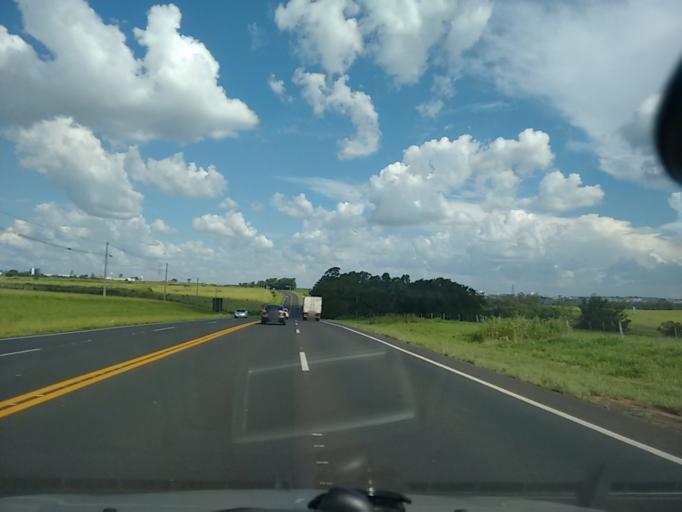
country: BR
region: Sao Paulo
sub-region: Marilia
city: Marilia
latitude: -22.1713
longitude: -49.9840
